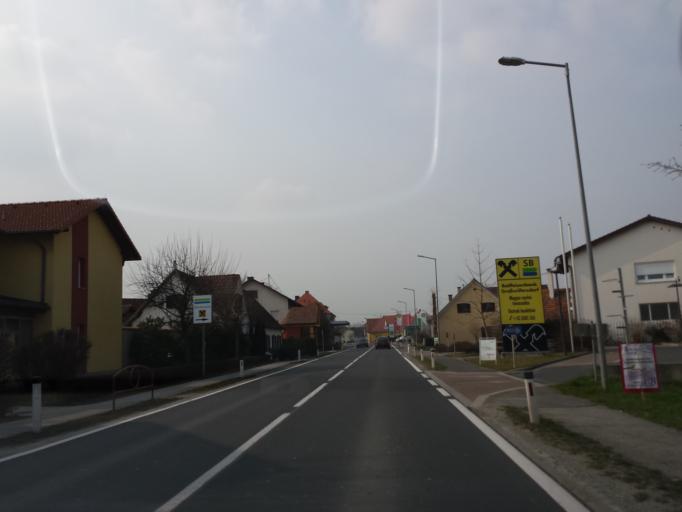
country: AT
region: Styria
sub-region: Politischer Bezirk Hartberg-Fuerstenfeld
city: Soechau
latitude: 47.0761
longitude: 15.9979
